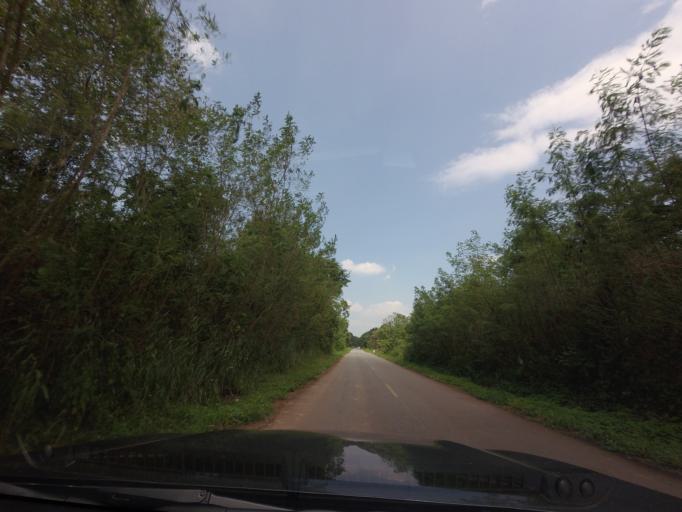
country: TH
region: Uttaradit
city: Fak Tha
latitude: 17.8456
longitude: 100.9498
